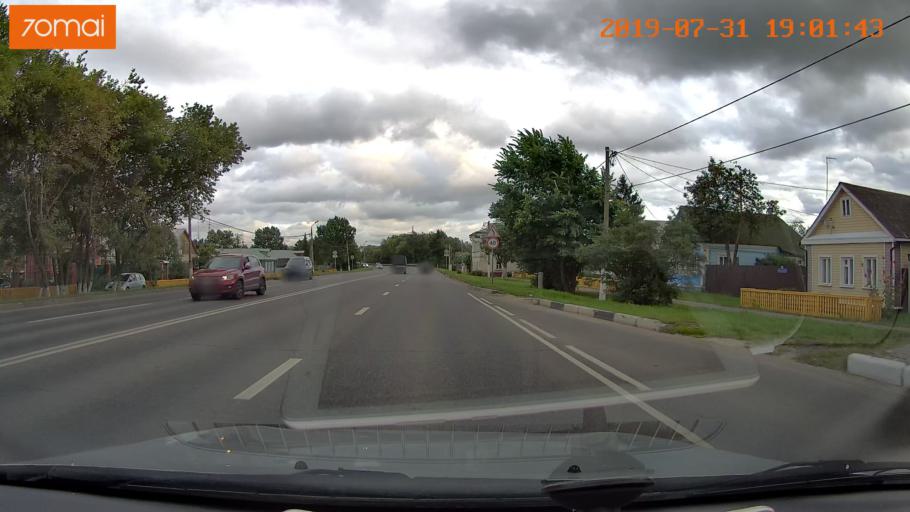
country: RU
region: Moskovskaya
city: Raduzhnyy
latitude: 55.1246
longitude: 38.7293
